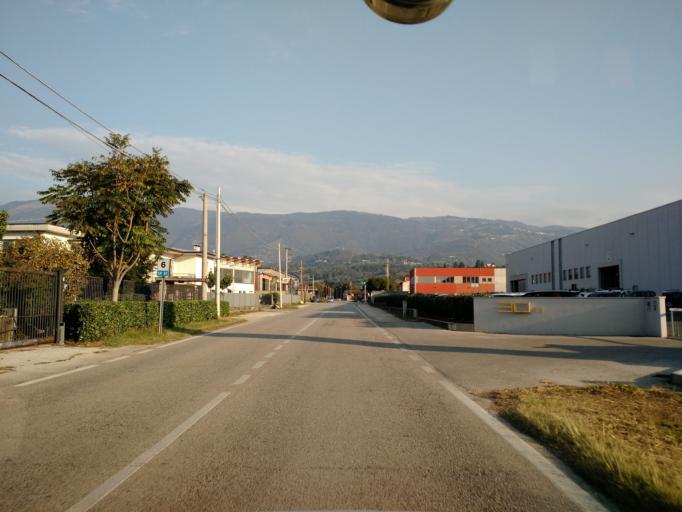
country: IT
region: Veneto
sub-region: Provincia di Vicenza
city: Fara Vicentino
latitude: 45.7300
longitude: 11.5425
